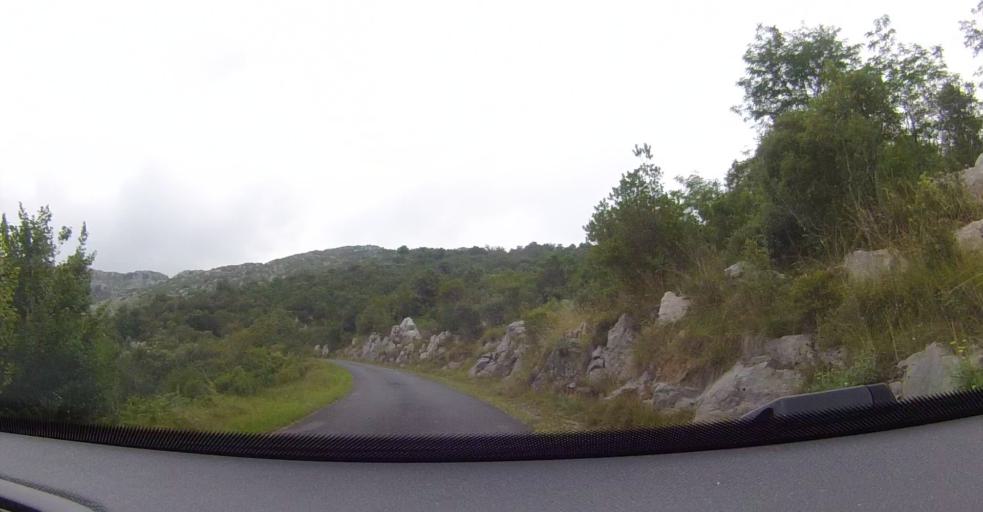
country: ES
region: Cantabria
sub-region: Provincia de Cantabria
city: Rasines
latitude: 43.2643
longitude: -3.3778
